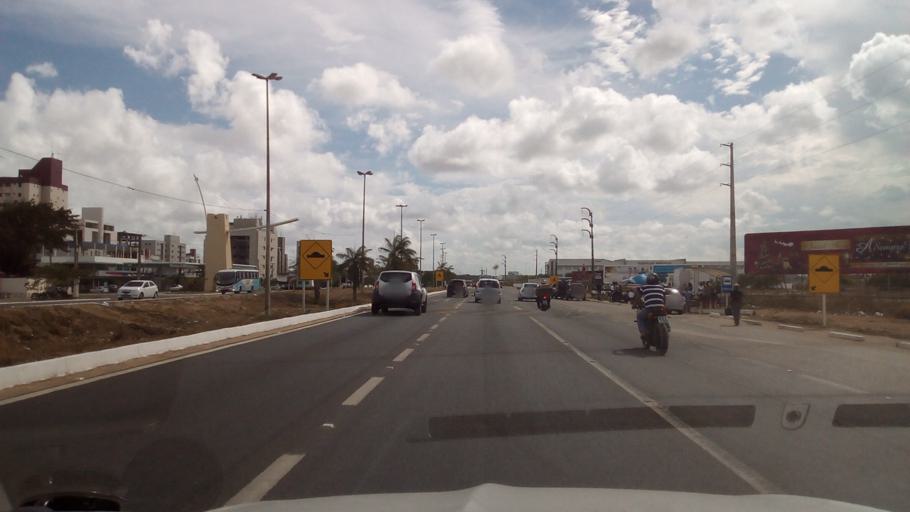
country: BR
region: Paraiba
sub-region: Cabedelo
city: Cabedelo
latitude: -7.0419
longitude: -34.8460
